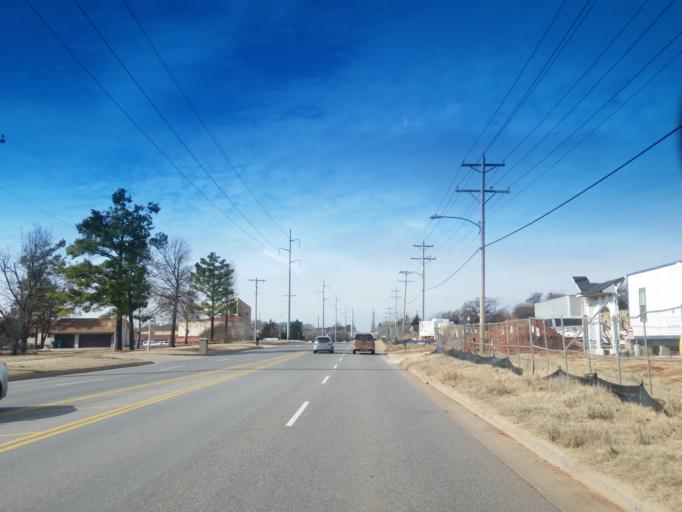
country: US
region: Oklahoma
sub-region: Oklahoma County
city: Edmond
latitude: 35.6673
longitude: -97.4442
